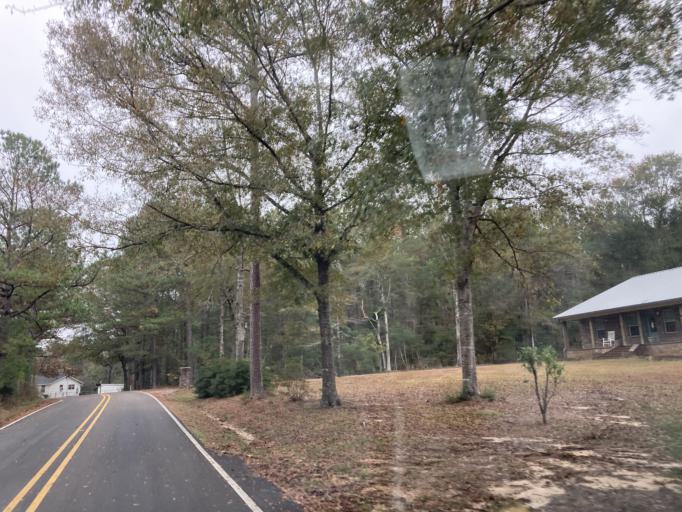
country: US
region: Mississippi
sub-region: Lamar County
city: Lumberton
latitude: 31.0650
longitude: -89.4189
